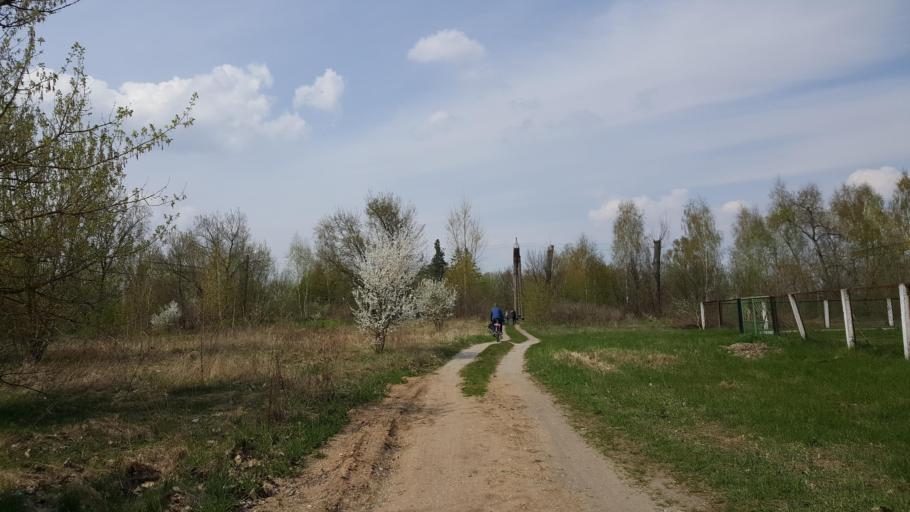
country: BY
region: Brest
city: Zhabinka
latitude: 52.1934
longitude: 24.0013
